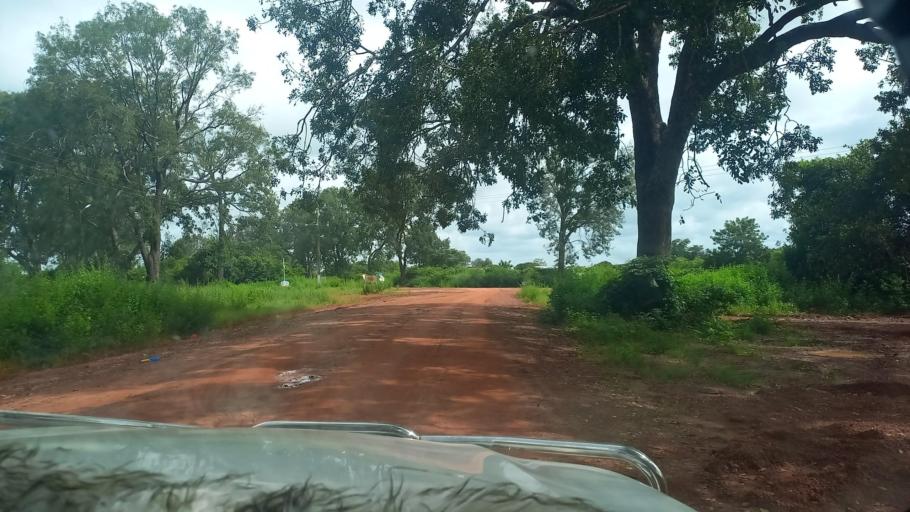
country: SN
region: Ziguinchor
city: Bignona
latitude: 12.7800
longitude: -16.2435
